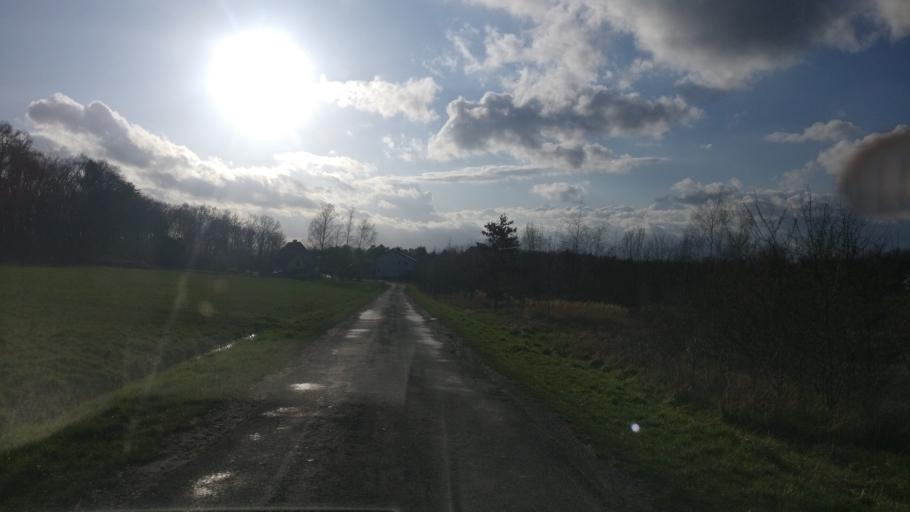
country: DE
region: North Rhine-Westphalia
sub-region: Regierungsbezirk Detmold
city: Lage
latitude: 52.0065
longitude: 8.7839
